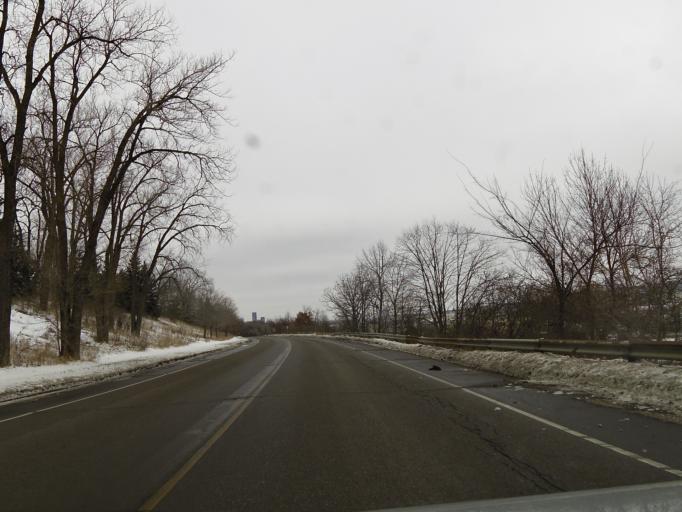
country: US
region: Minnesota
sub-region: Dakota County
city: South Saint Paul
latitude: 44.9212
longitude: -93.0609
